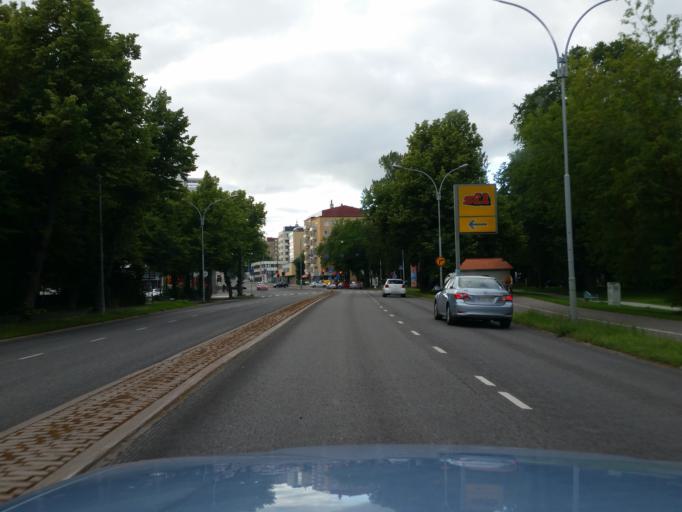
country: FI
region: Varsinais-Suomi
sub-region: Turku
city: Turku
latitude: 60.4449
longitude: 22.2853
